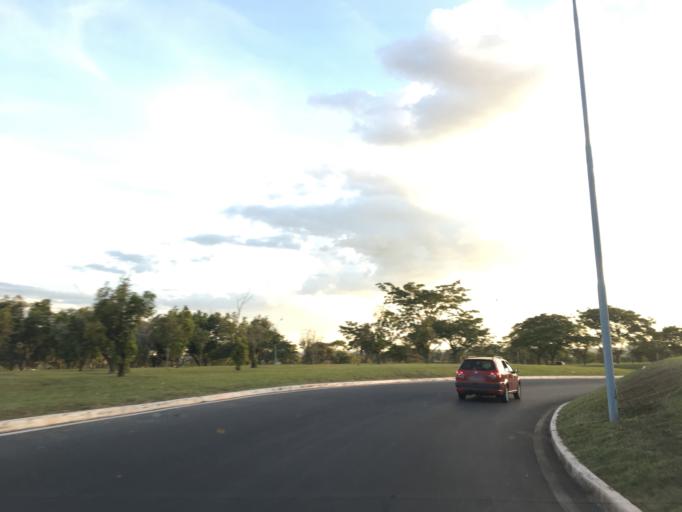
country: BR
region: Federal District
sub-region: Brasilia
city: Brasilia
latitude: -15.8364
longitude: -47.9247
